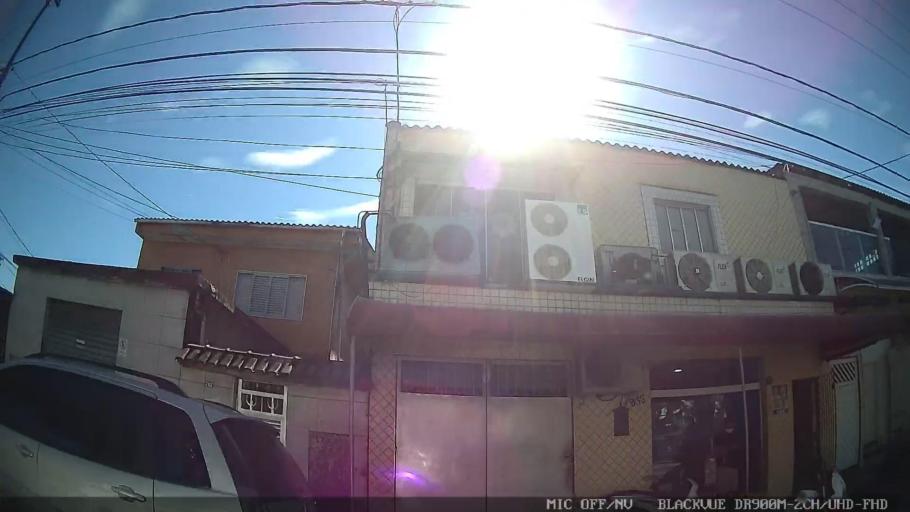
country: BR
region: Sao Paulo
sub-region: Santos
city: Santos
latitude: -23.9501
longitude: -46.2854
